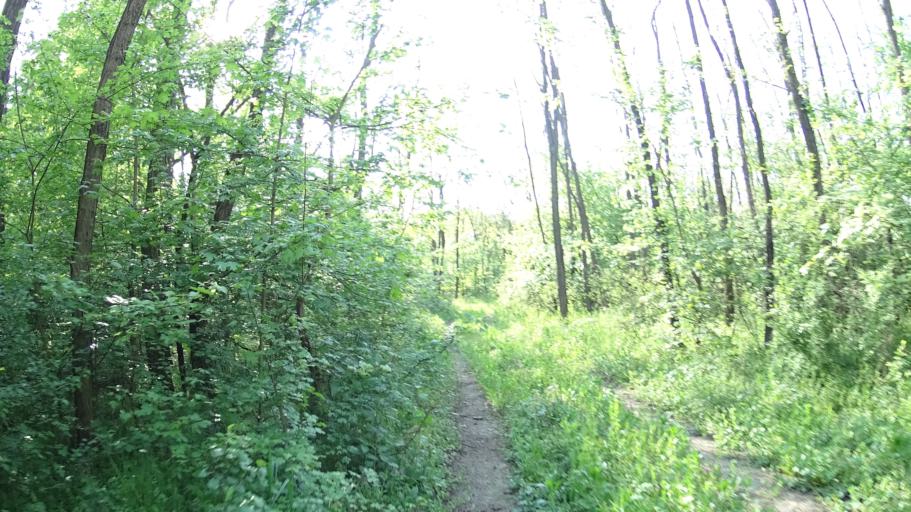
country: HU
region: Nograd
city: Retsag
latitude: 47.9132
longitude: 19.1698
